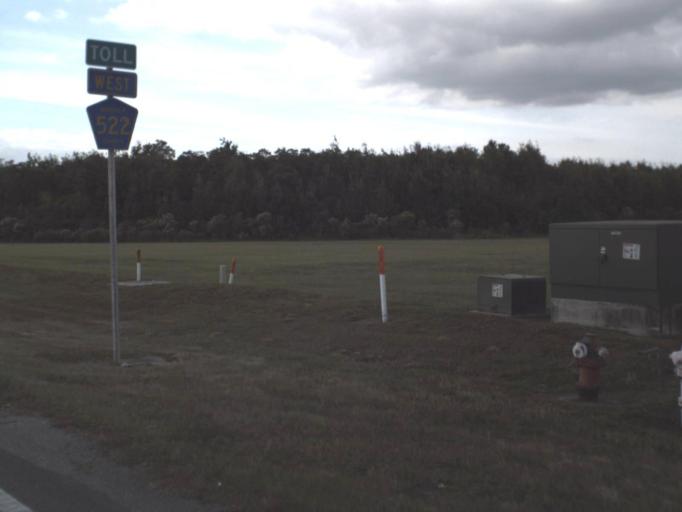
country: US
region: Florida
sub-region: Orange County
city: Hunters Creek
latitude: 28.3420
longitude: -81.4312
